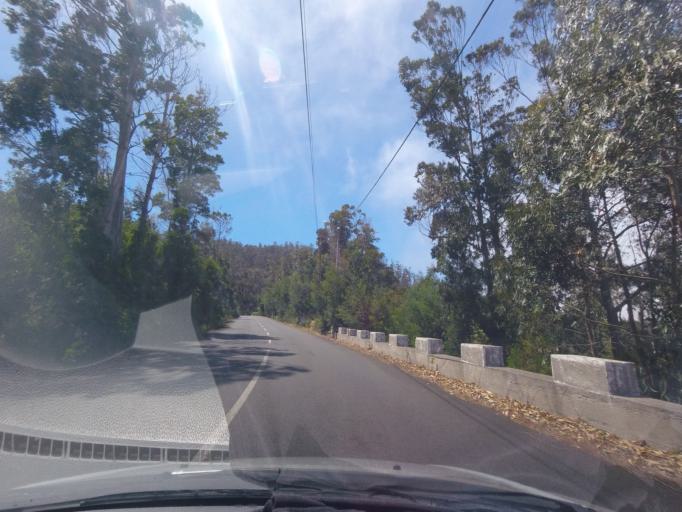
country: PT
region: Madeira
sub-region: Santa Cruz
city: Camacha
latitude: 32.6864
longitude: -16.8273
